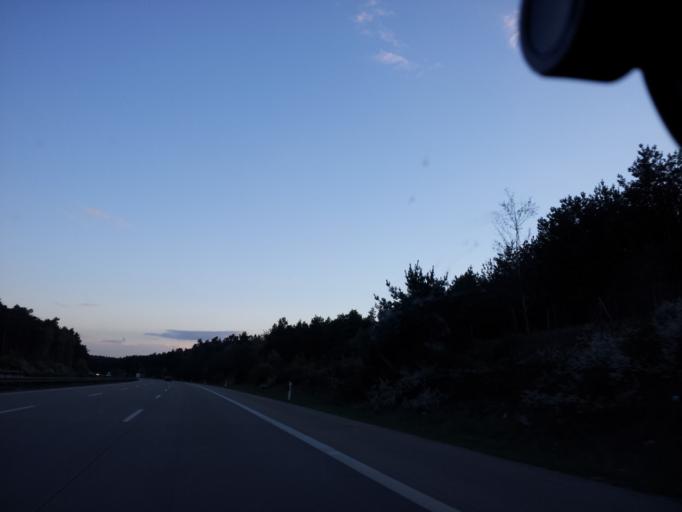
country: DE
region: Brandenburg
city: Erkner
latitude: 52.3691
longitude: 13.7650
